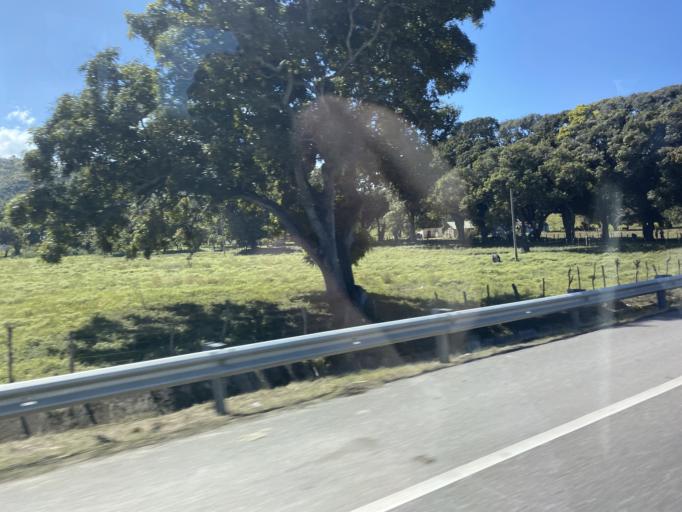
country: DO
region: Puerto Plata
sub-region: Puerto Plata
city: Puerto Plata
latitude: 19.8299
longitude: -70.7635
